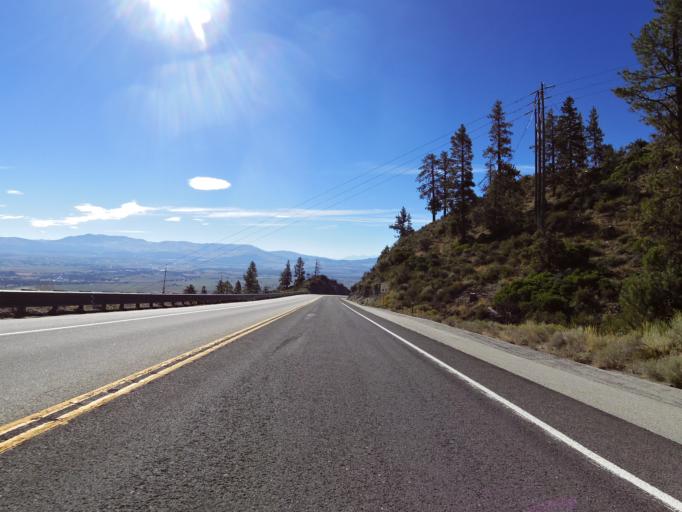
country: US
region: Nevada
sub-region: Douglas County
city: Kingsbury
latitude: 38.9718
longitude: -119.8546
